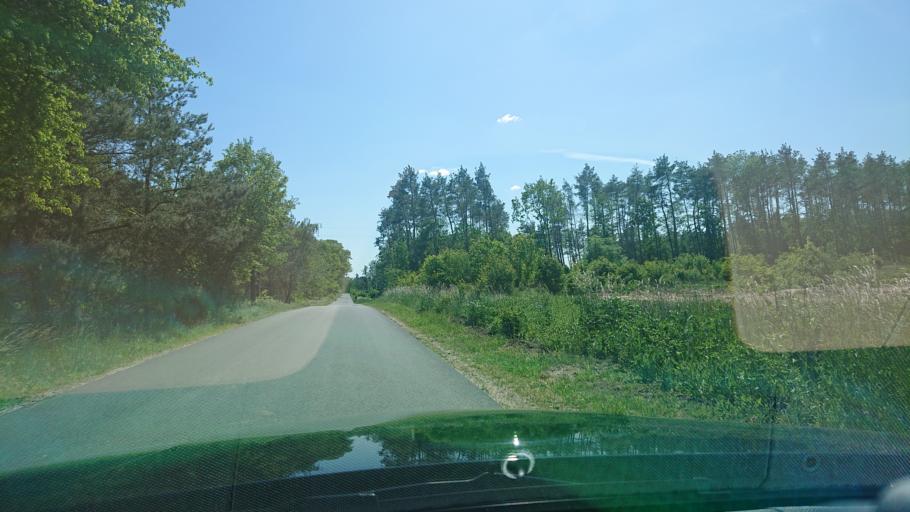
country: PL
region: Greater Poland Voivodeship
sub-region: Powiat gnieznienski
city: Gniezno
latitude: 52.4973
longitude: 17.5818
